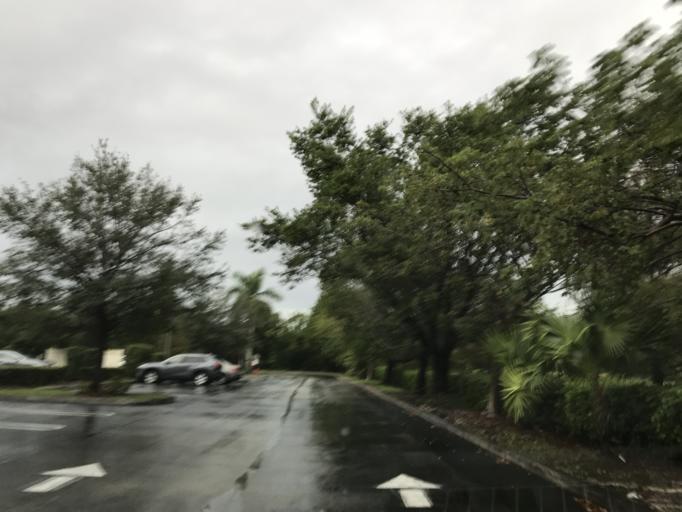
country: US
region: Florida
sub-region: Broward County
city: Coral Springs
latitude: 26.3065
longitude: -80.2817
